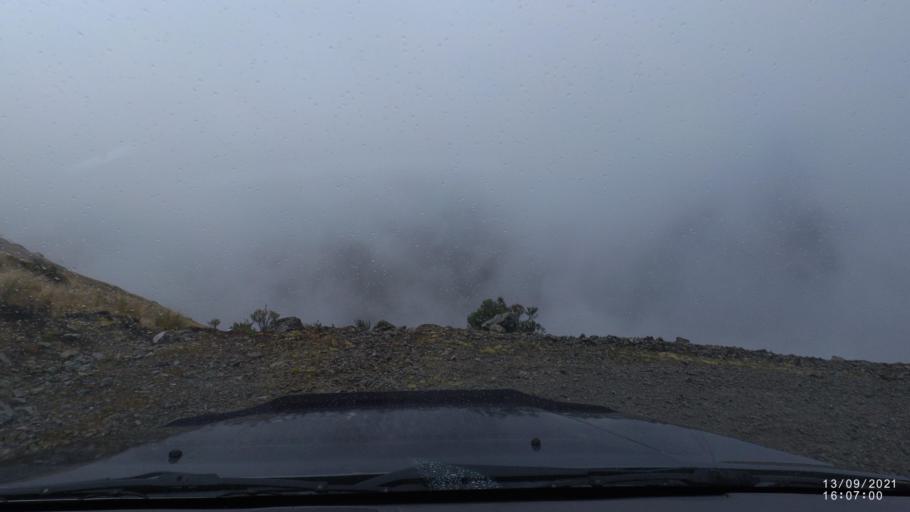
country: BO
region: Cochabamba
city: Colomi
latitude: -17.2809
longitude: -65.7097
